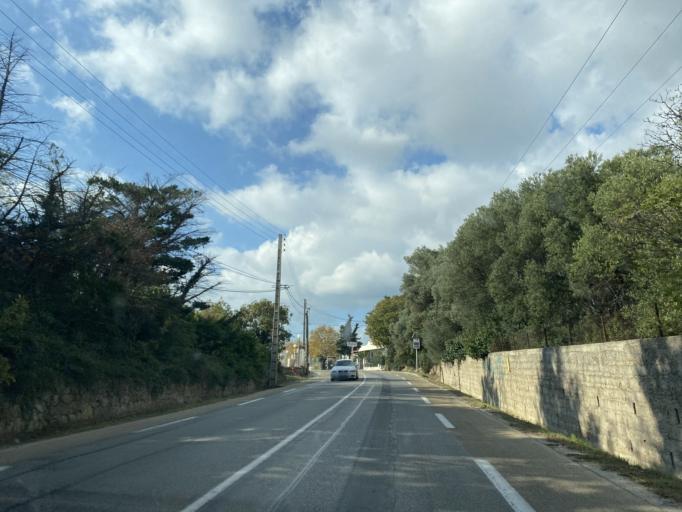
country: FR
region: Provence-Alpes-Cote d'Azur
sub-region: Departement du Var
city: Ollioules
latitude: 43.1274
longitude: 5.8619
